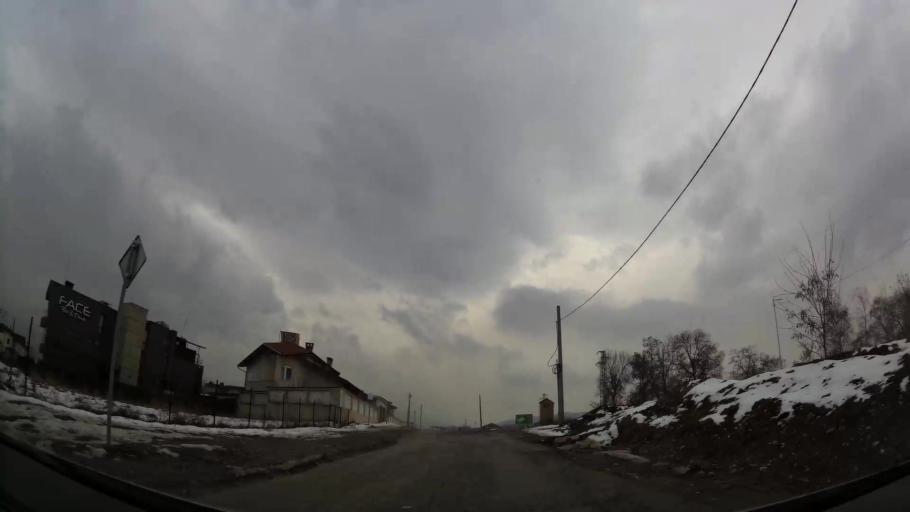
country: BG
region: Sofiya
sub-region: Obshtina Bozhurishte
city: Bozhurishte
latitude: 42.6713
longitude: 23.2205
